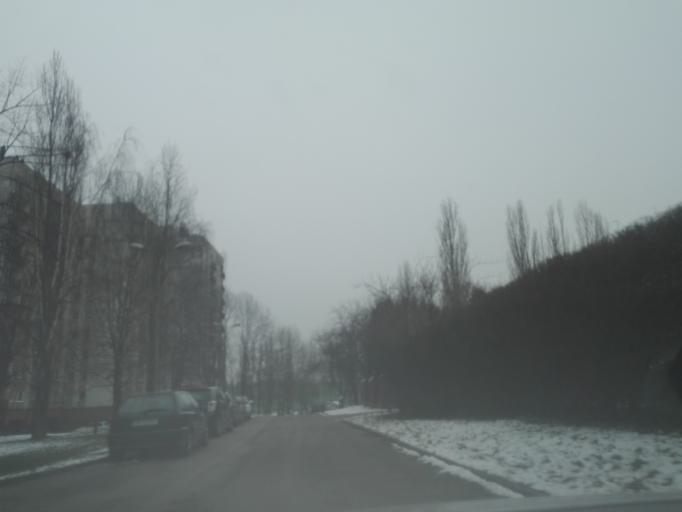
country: PL
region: Silesian Voivodeship
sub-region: Katowice
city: Katowice
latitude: 50.2475
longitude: 19.0318
